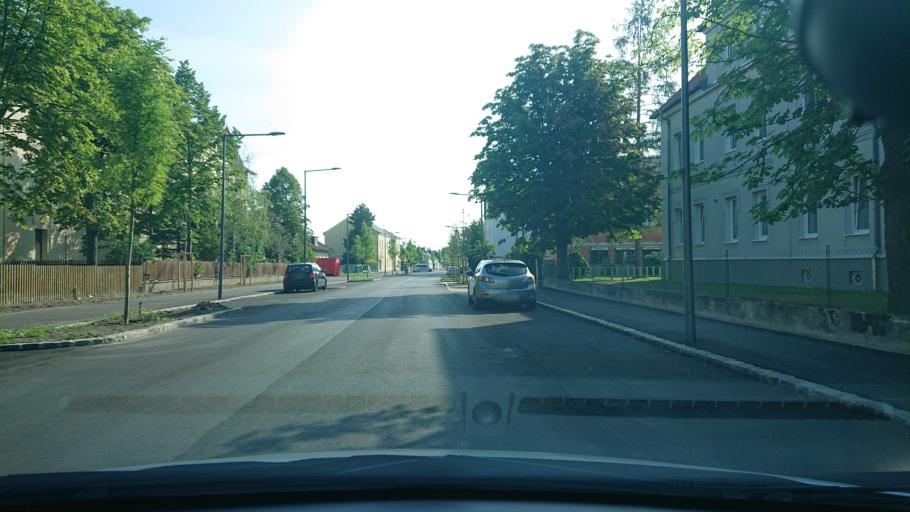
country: AT
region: Lower Austria
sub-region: Politischer Bezirk Baden
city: Leobersdorf
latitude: 47.9331
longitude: 16.2224
